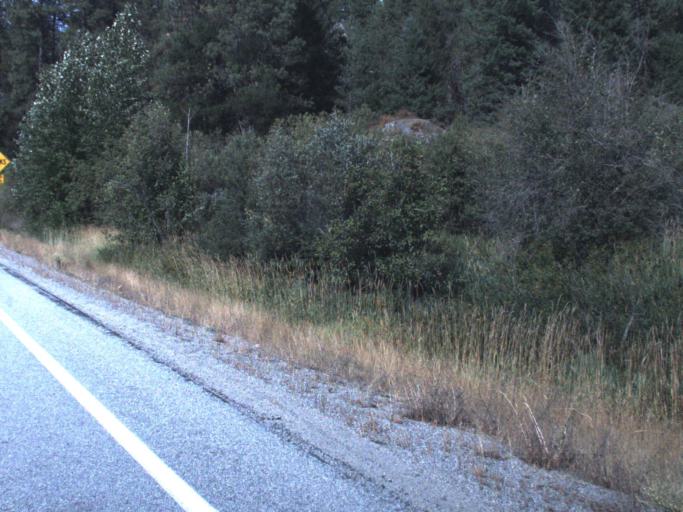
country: US
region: Washington
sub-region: Pend Oreille County
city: Newport
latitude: 48.2118
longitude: -117.2906
